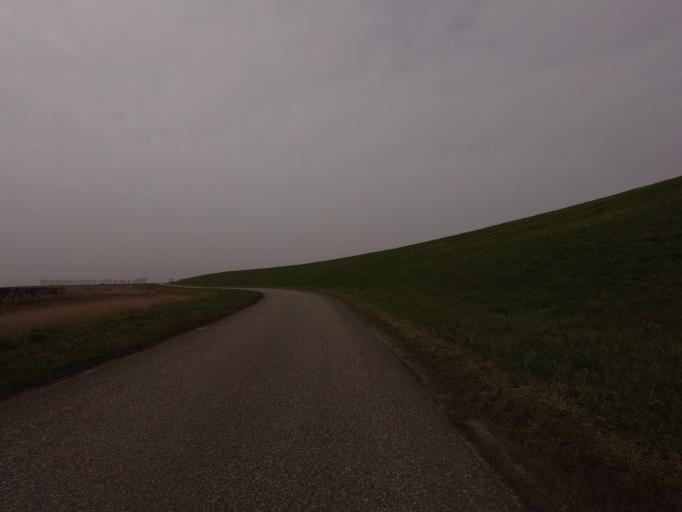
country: NL
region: Zeeland
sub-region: Gemeente Hulst
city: Hulst
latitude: 51.3428
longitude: 4.1229
